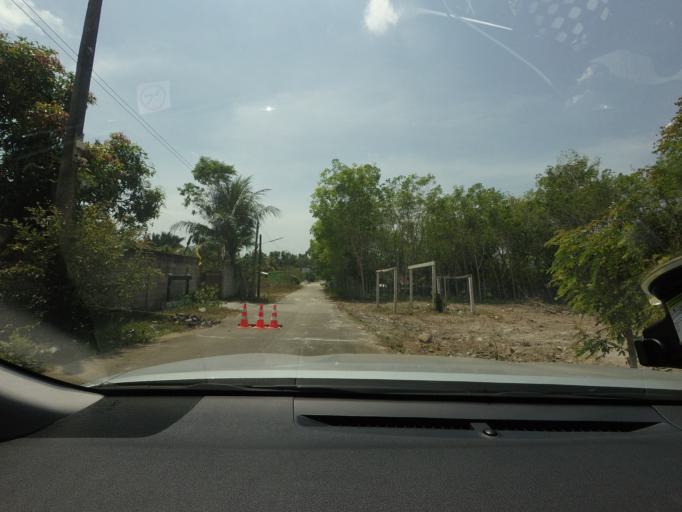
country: TH
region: Narathiwat
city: Rueso
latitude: 6.3827
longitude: 101.5095
